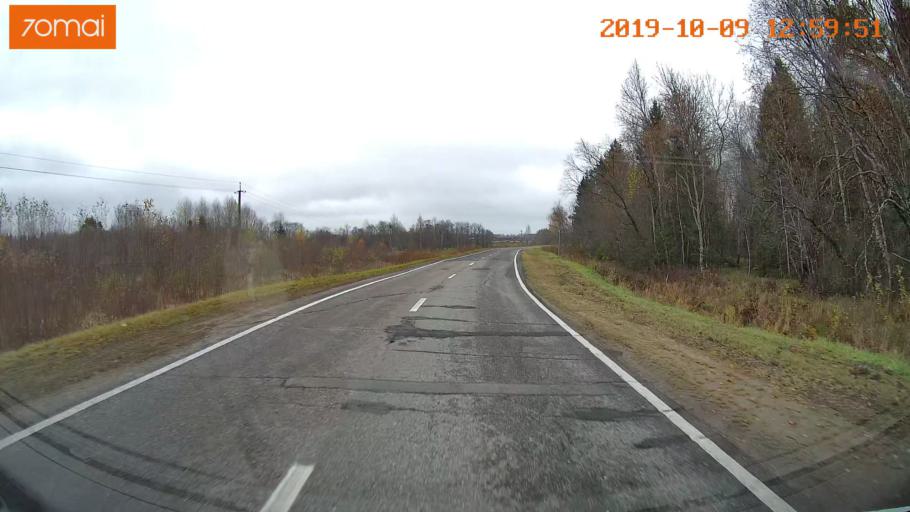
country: RU
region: Jaroslavl
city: Prechistoye
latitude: 58.3817
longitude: 40.4715
